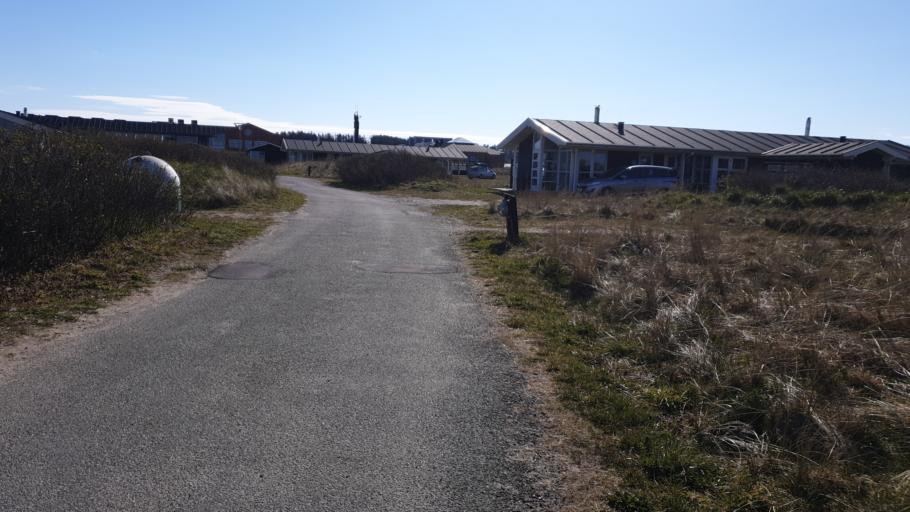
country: DK
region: North Denmark
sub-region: Hjorring Kommune
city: Hjorring
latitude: 57.4940
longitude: 9.8335
